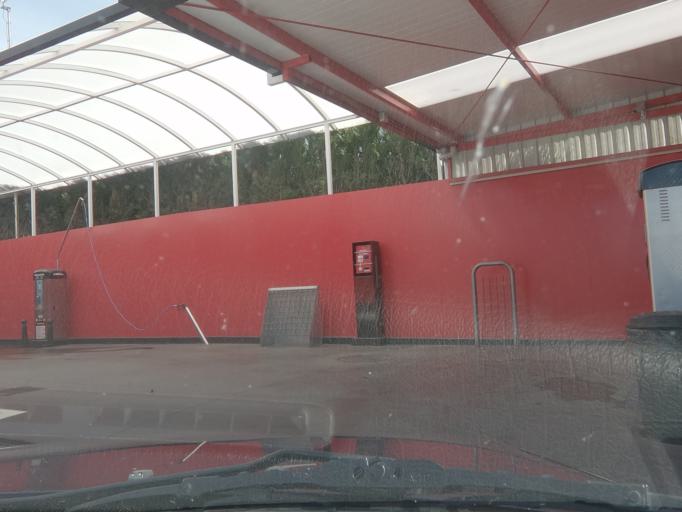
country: ES
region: Galicia
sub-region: Provincia da Coruna
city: Santiago de Compostela
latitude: 42.9021
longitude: -8.5203
